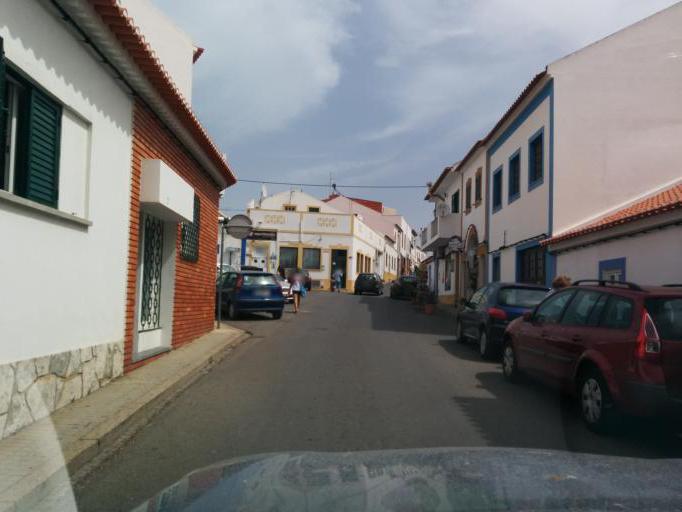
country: PT
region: Beja
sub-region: Odemira
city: Vila Nova de Milfontes
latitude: 37.7245
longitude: -8.7816
